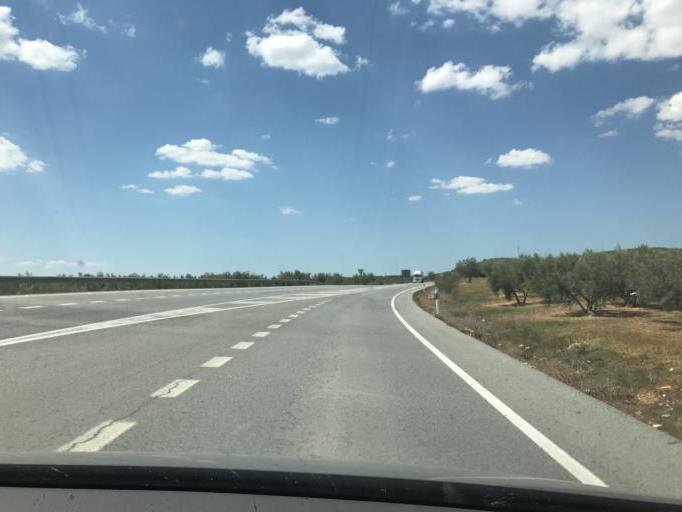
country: ES
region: Andalusia
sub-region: Provincia de Jaen
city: Frailes
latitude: 37.4374
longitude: -3.8158
